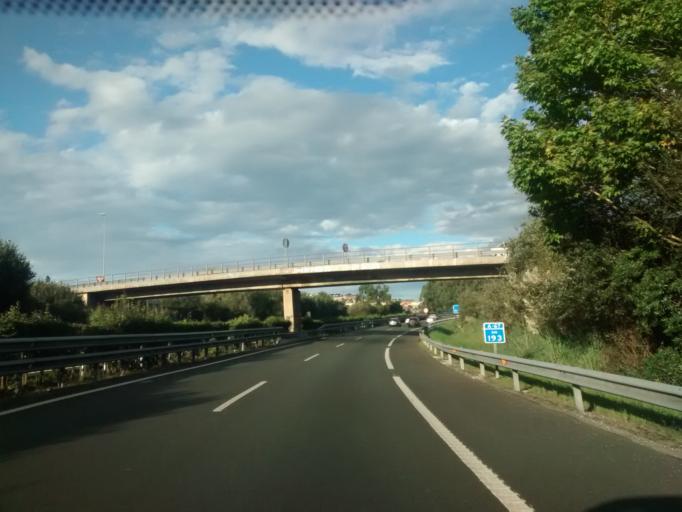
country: ES
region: Cantabria
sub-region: Provincia de Cantabria
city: Miengo
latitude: 43.4186
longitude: -3.9601
